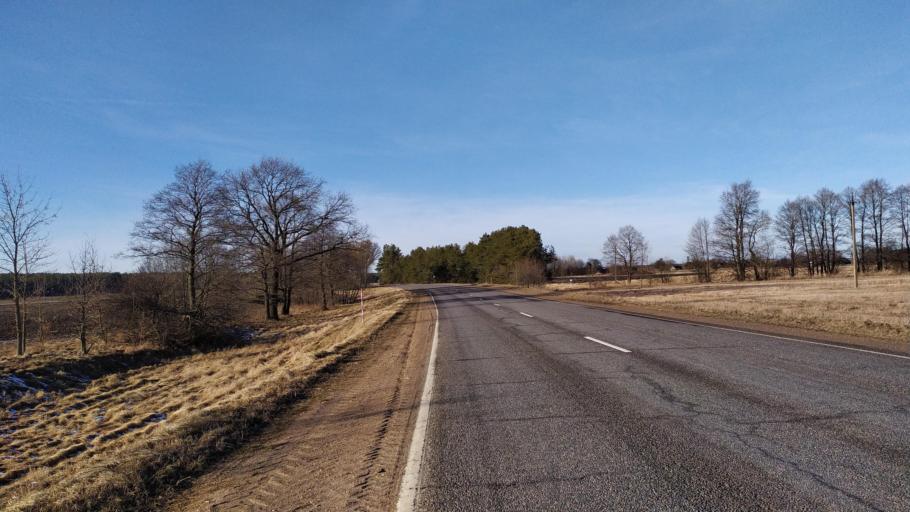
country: BY
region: Brest
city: Kamyanyets
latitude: 52.3698
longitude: 23.8844
